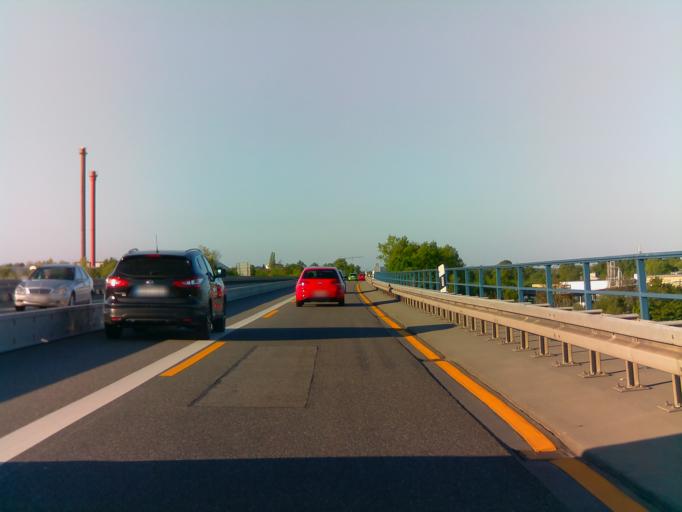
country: DE
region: Baden-Wuerttemberg
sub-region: Karlsruhe Region
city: Dossenheim
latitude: 49.4405
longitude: 8.6429
